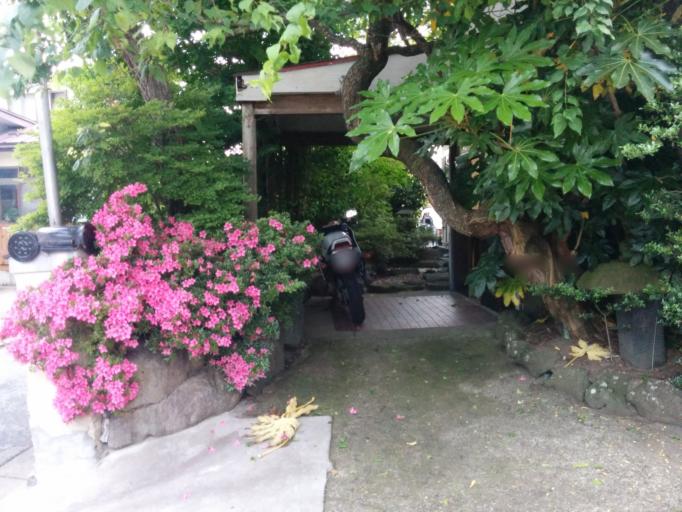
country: JP
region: Akita
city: Akita
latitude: 39.7252
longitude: 140.1214
